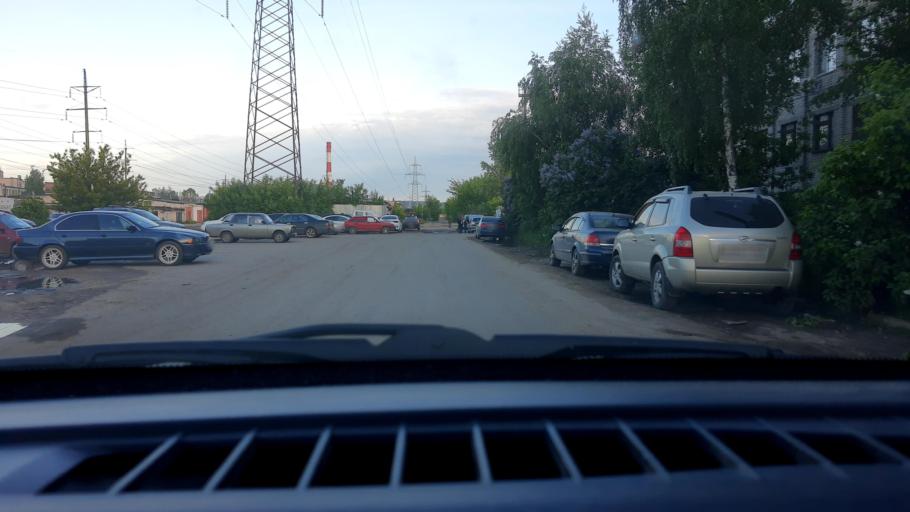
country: RU
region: Nizjnij Novgorod
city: Nizhniy Novgorod
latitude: 56.2754
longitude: 43.8956
